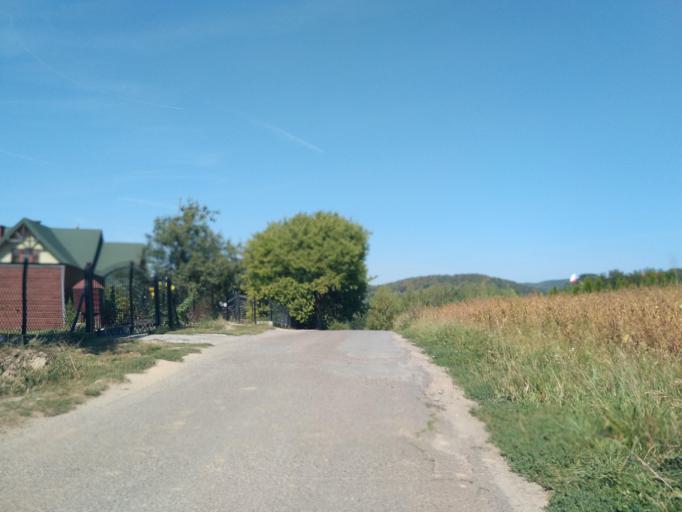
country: PL
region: Subcarpathian Voivodeship
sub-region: Powiat brzozowski
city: Grabownica Starzenska
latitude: 49.6563
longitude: 22.0848
